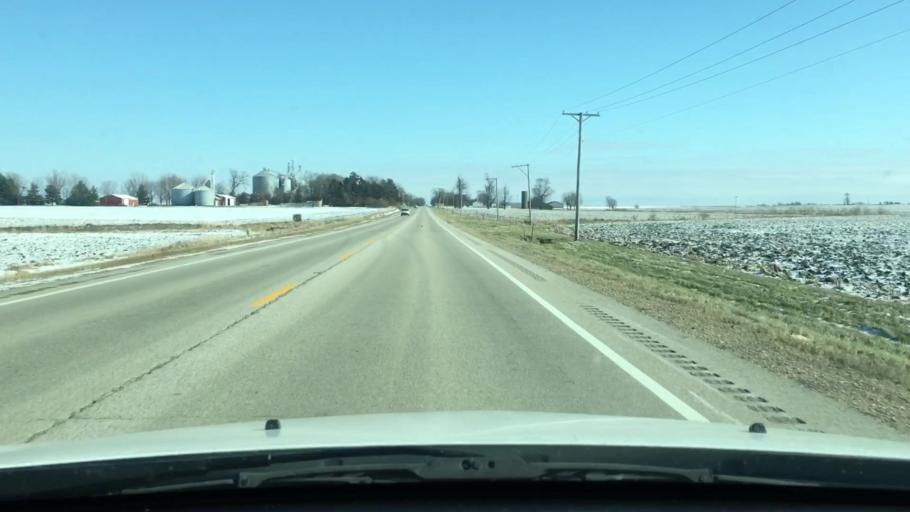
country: US
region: Illinois
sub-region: DeKalb County
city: Malta
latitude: 42.0013
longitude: -88.8357
